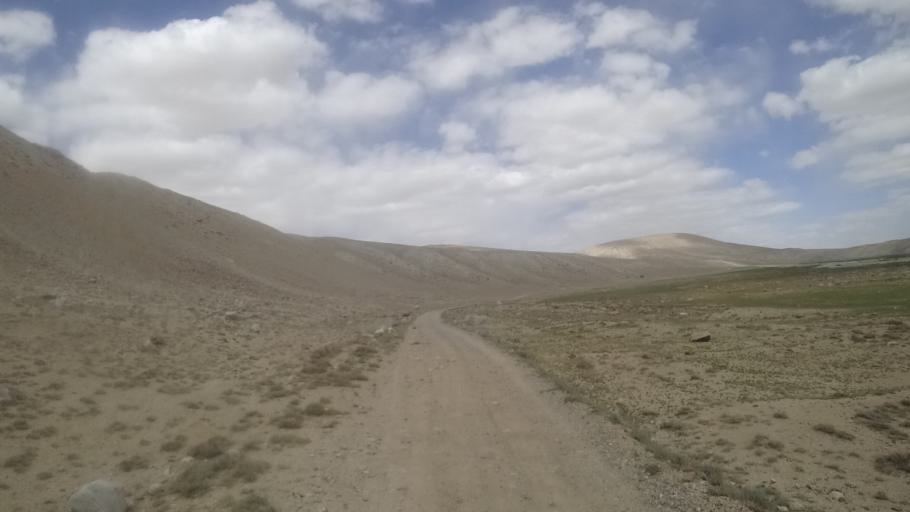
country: AF
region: Badakhshan
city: Khandud
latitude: 37.4054
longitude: 73.1488
